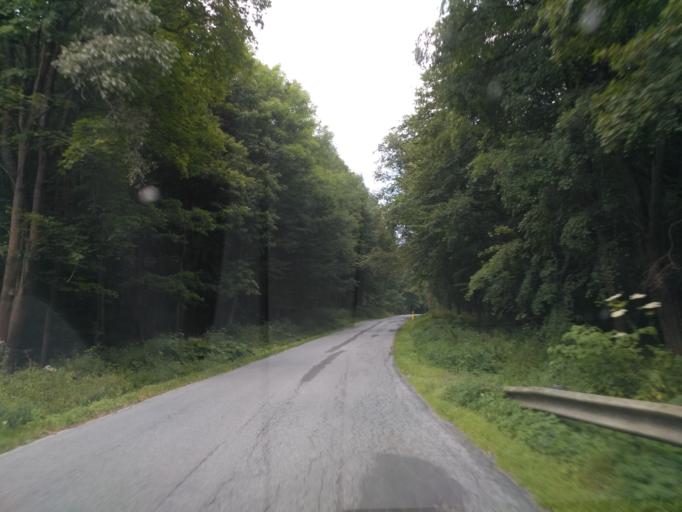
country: SK
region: Kosicky
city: Gelnica
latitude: 48.9185
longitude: 21.0350
